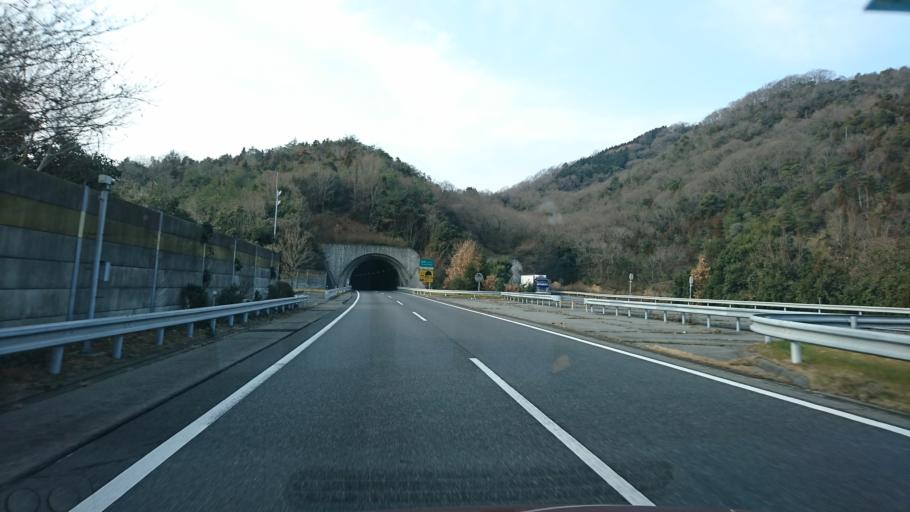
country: JP
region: Okayama
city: Okayama-shi
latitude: 34.7676
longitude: 134.0657
